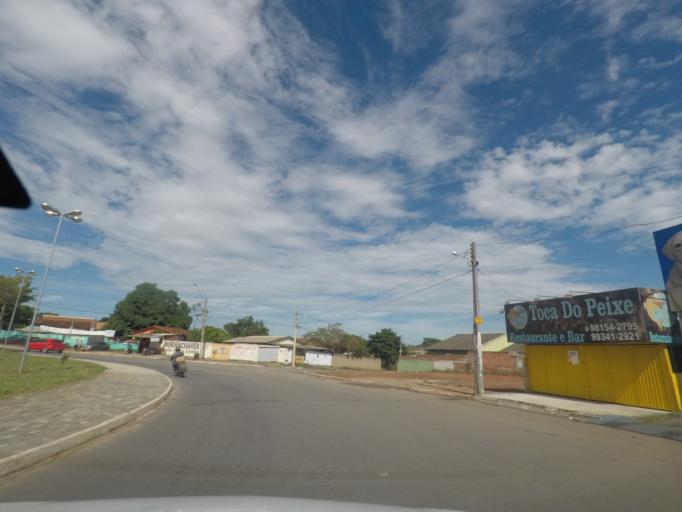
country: BR
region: Goias
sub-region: Aparecida De Goiania
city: Aparecida de Goiania
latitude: -16.7973
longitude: -49.2836
